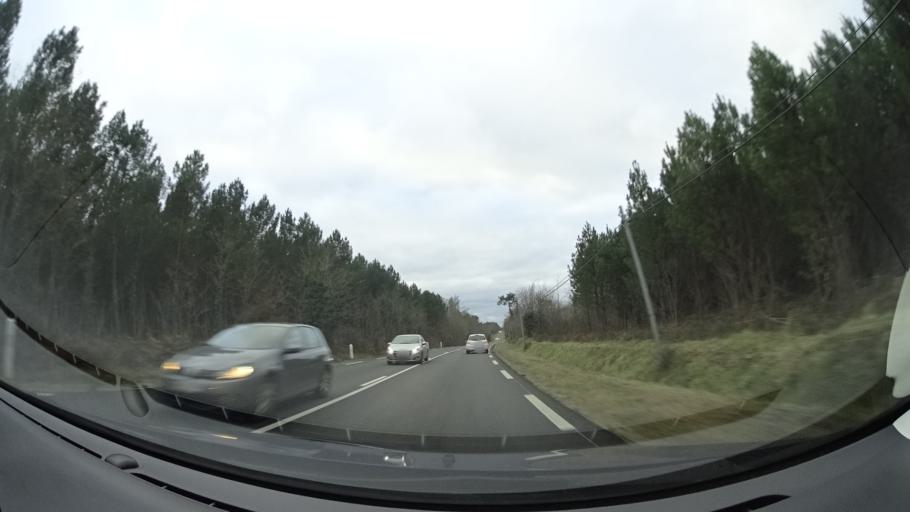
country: FR
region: Aquitaine
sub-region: Departement des Landes
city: Sarbazan
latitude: 43.9581
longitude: -0.3335
